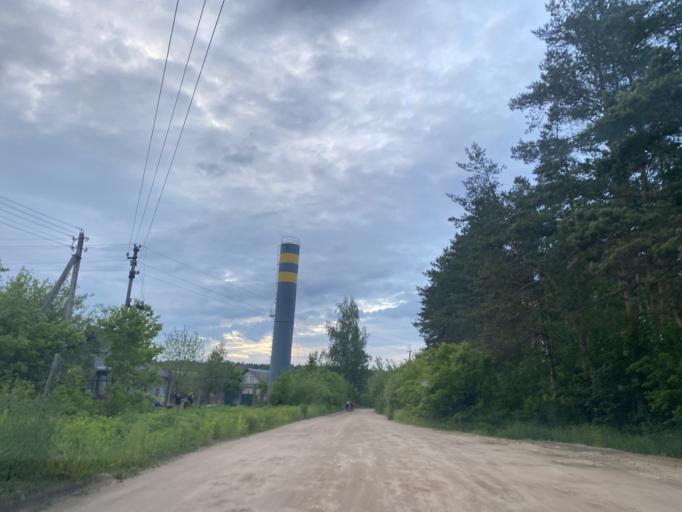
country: BY
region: Minsk
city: Rudzyensk
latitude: 53.6083
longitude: 27.7927
